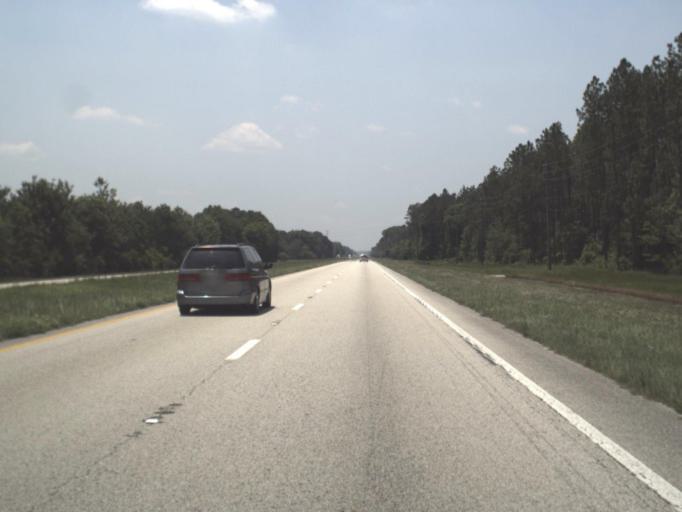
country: US
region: Florida
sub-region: Duval County
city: Baldwin
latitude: 30.2156
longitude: -82.0094
